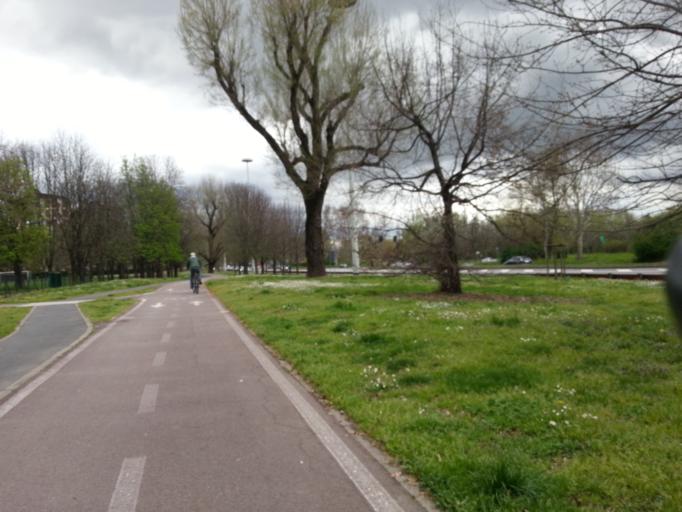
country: IT
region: Lombardy
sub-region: Citta metropolitana di Milano
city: Bresso
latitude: 45.5126
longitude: 9.1793
